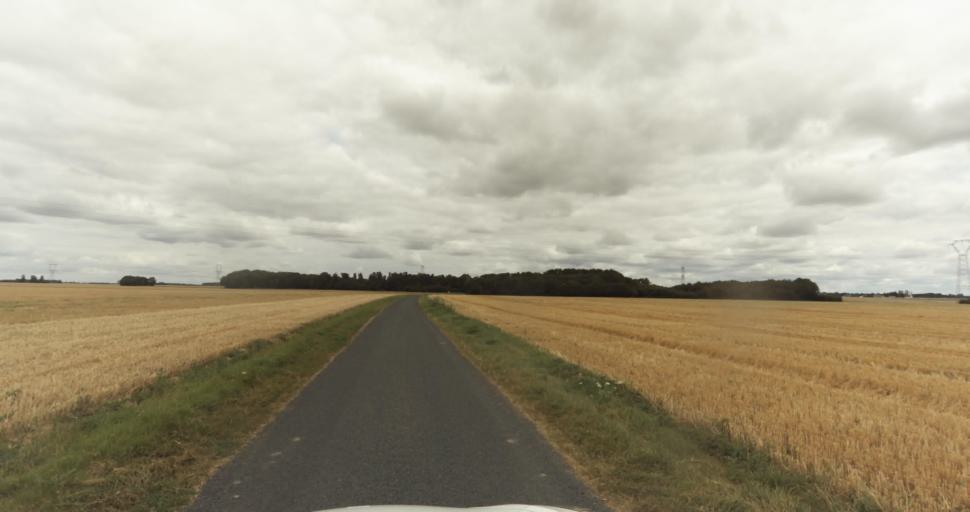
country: FR
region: Haute-Normandie
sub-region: Departement de l'Eure
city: La Madeleine-de-Nonancourt
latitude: 48.8407
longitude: 1.2029
